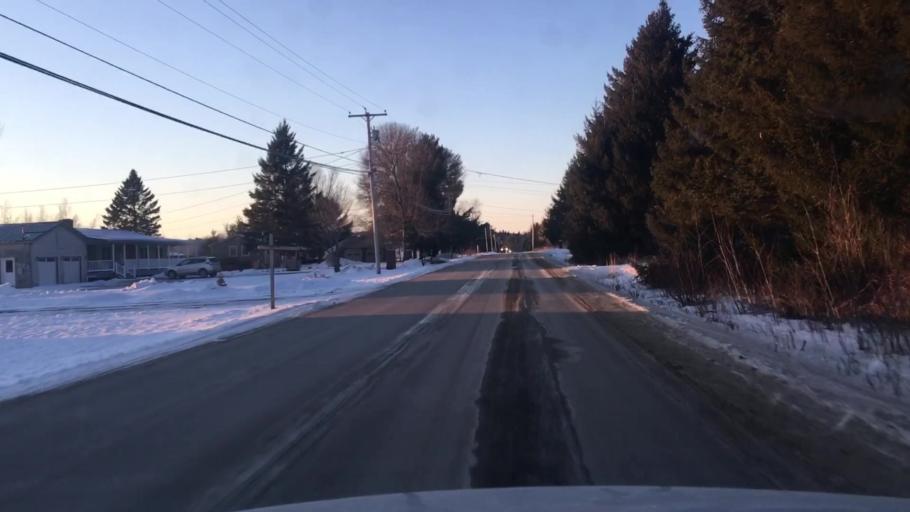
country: US
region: Maine
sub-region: Penobscot County
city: Brewer
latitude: 44.7318
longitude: -68.7601
